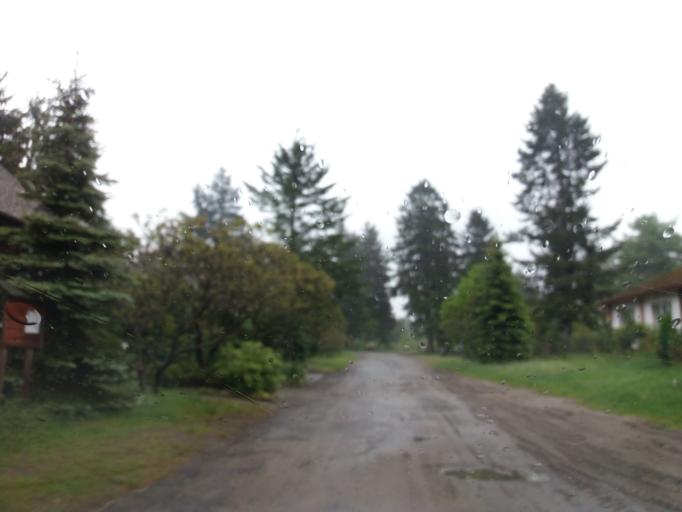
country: PL
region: West Pomeranian Voivodeship
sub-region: Powiat drawski
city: Kalisz Pomorski
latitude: 53.2078
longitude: 15.9705
